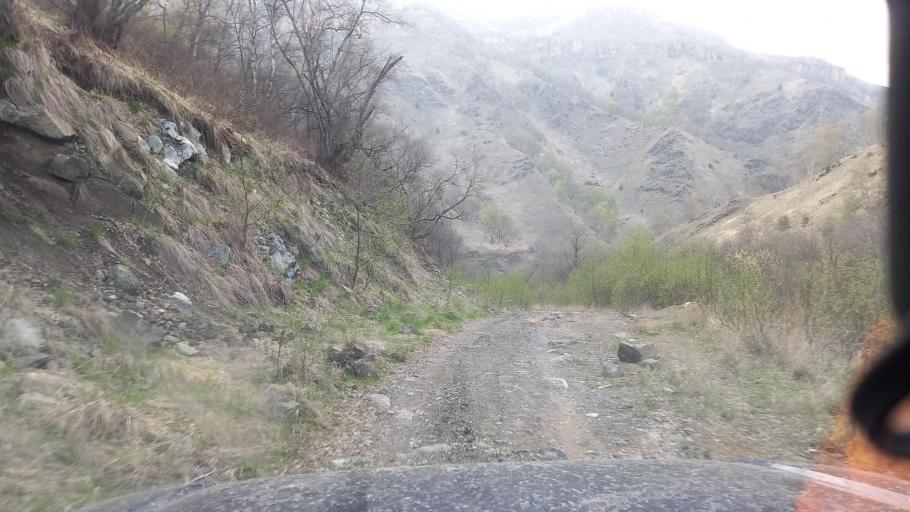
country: RU
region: Kabardino-Balkariya
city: Kamennomostskoye
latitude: 43.6952
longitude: 42.8437
